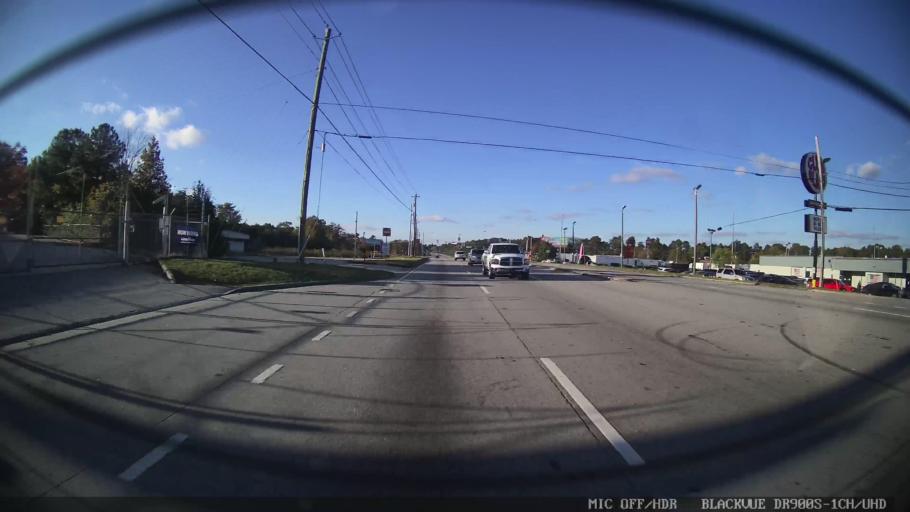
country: US
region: Georgia
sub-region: Clayton County
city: Conley
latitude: 33.6560
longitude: -84.3344
